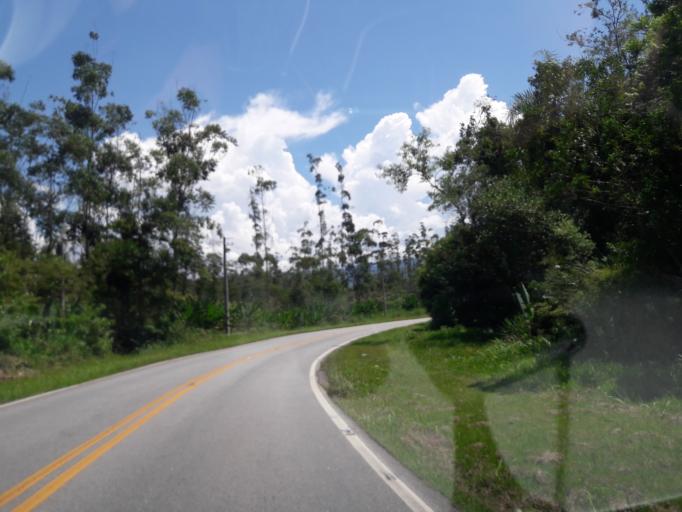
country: BR
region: Parana
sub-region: Antonina
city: Antonina
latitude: -25.5267
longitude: -48.7770
